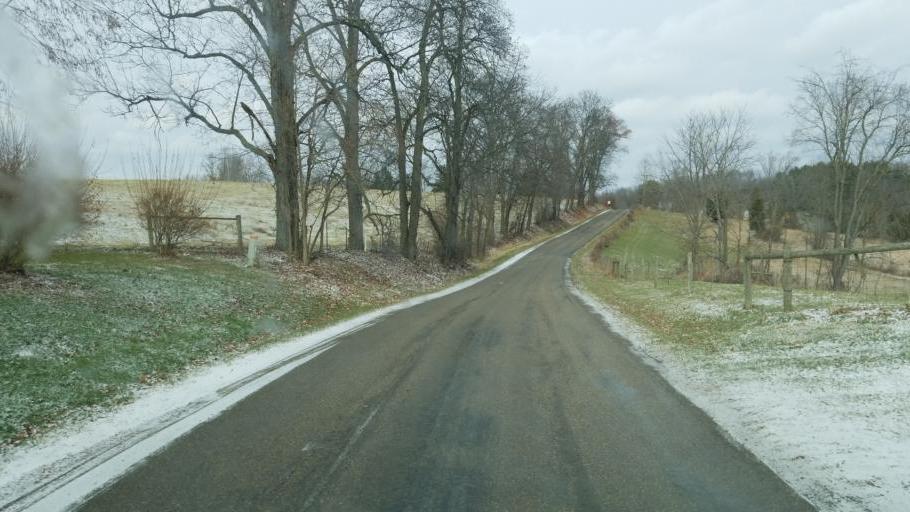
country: US
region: Ohio
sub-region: Muskingum County
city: Frazeysburg
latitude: 40.1435
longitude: -82.1577
